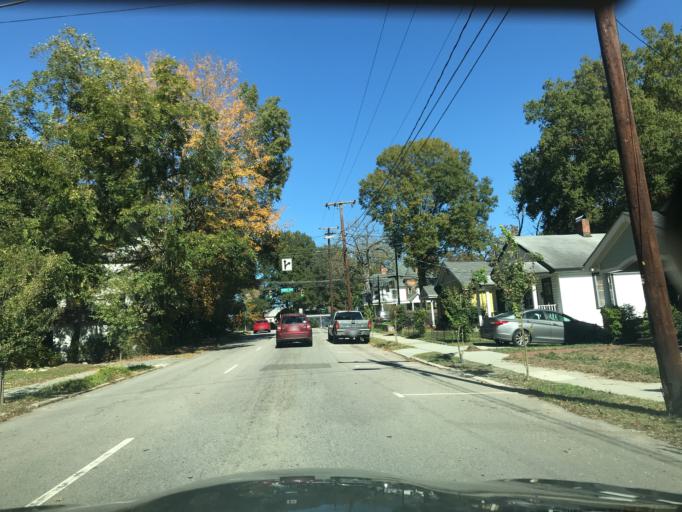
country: US
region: North Carolina
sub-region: Durham County
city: Durham
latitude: 36.0047
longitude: -78.8927
